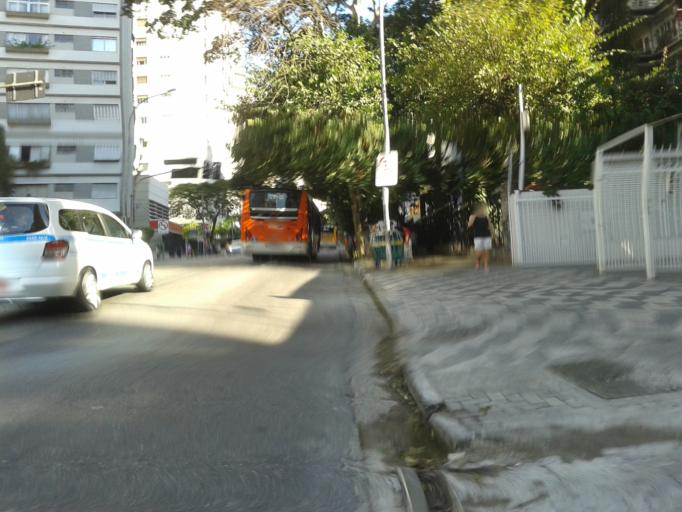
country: BR
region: Sao Paulo
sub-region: Sao Paulo
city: Sao Paulo
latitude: -23.5423
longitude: -46.6559
